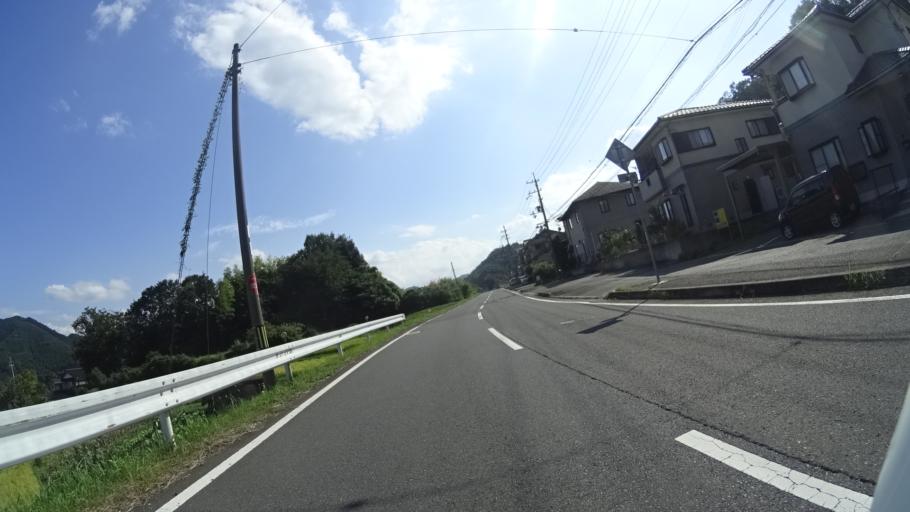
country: JP
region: Kyoto
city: Maizuru
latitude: 35.4551
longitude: 135.3064
